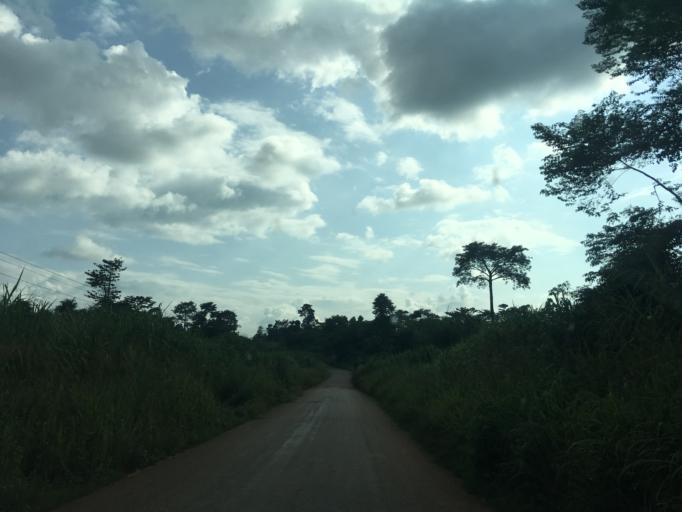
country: GH
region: Western
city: Bibiani
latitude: 6.7820
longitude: -2.5501
